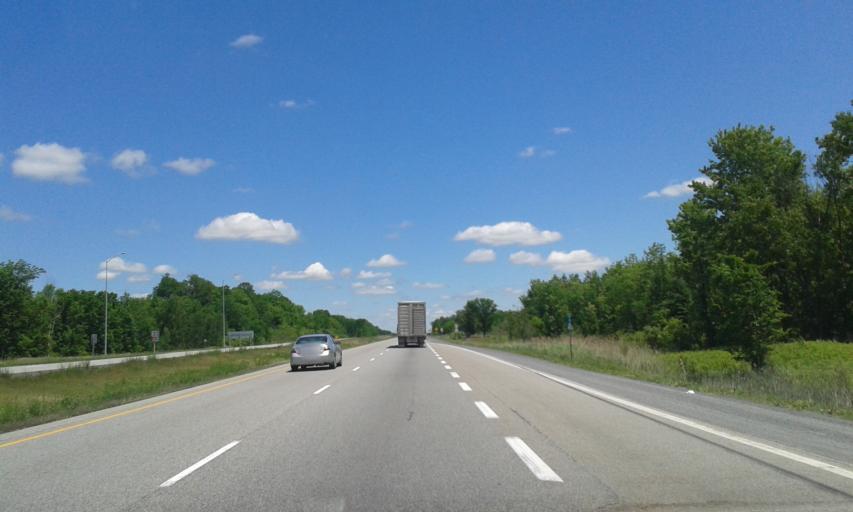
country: US
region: New York
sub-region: St. Lawrence County
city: Massena
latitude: 45.0470
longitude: -74.9060
